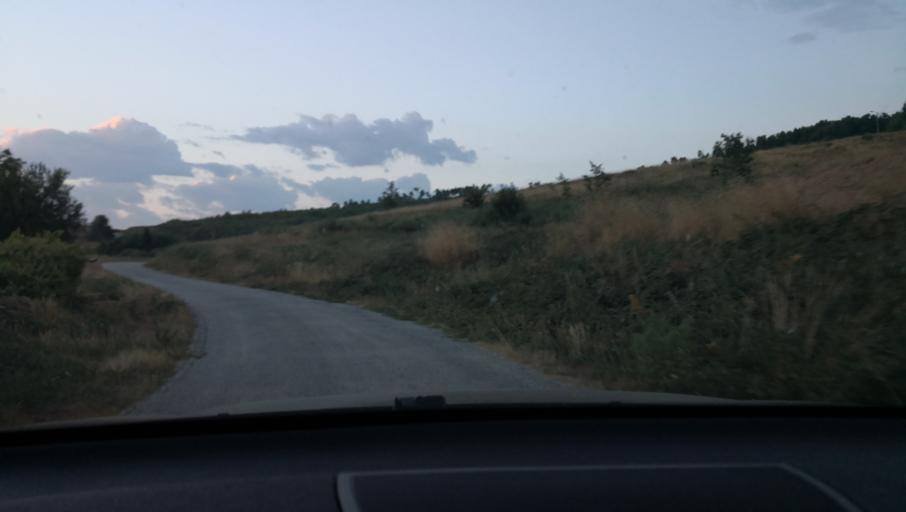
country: PT
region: Vila Real
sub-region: Sabrosa
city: Sabrosa
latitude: 41.2695
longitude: -7.6221
